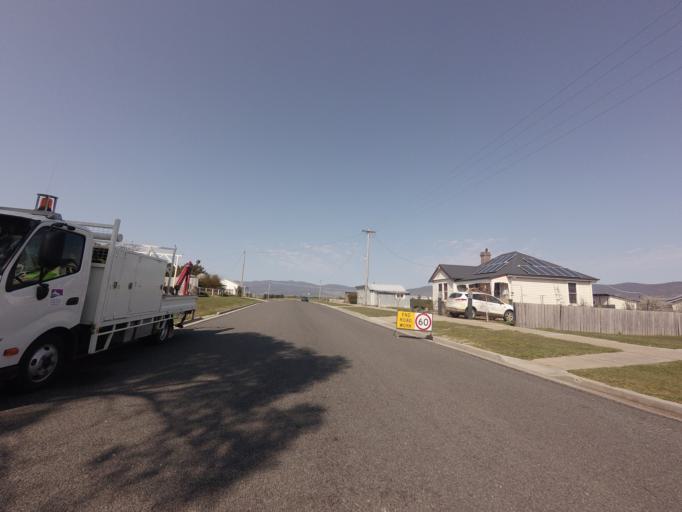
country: AU
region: Tasmania
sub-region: Northern Midlands
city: Evandale
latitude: -41.7825
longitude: 147.7230
